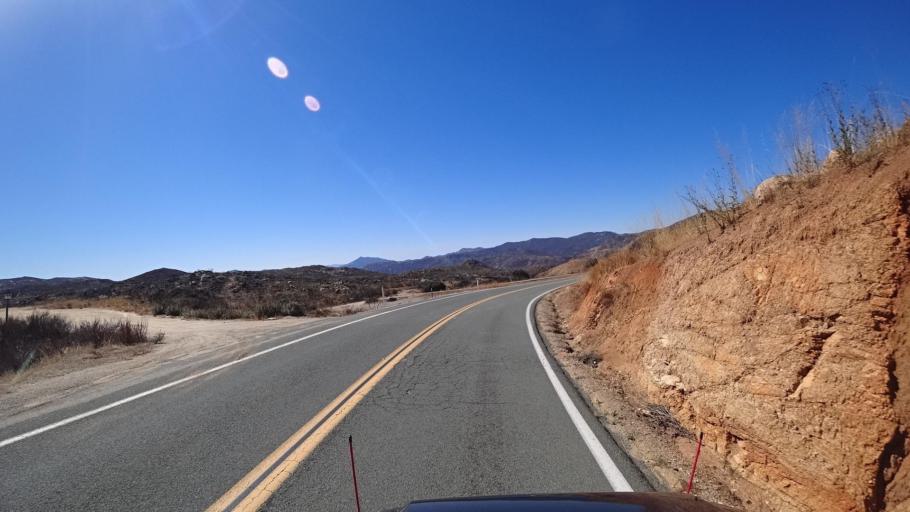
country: US
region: California
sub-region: San Diego County
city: Descanso
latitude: 32.7474
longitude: -116.6686
